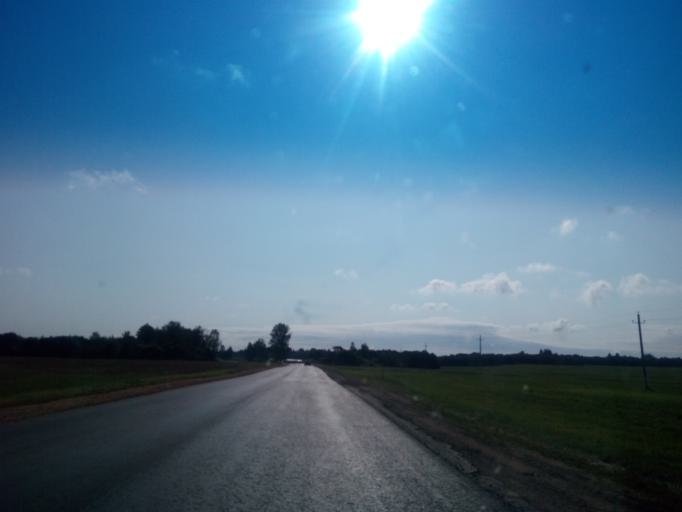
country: BY
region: Vitebsk
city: Vyerkhnyadzvinsk
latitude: 55.7245
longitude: 28.0321
